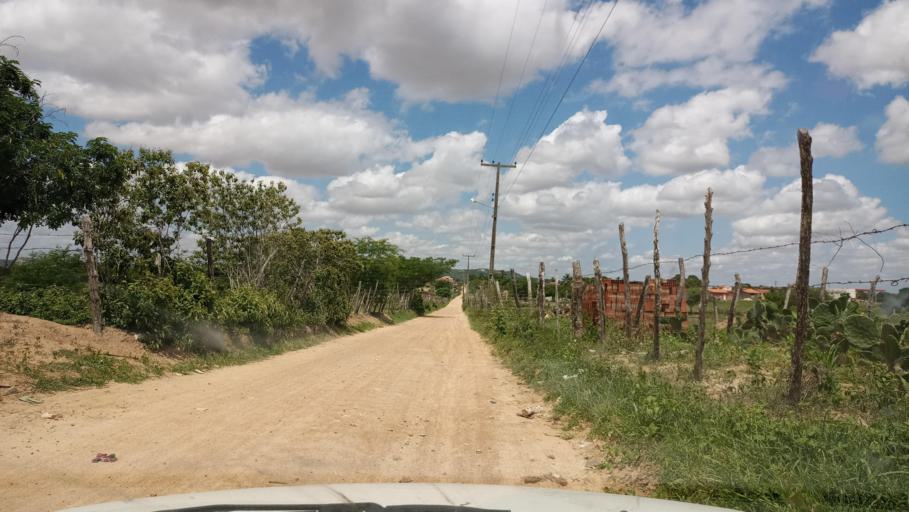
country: BR
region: Rio Grande do Norte
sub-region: Sao Jose Do Campestre
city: Sao Jose do Campestre
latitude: -6.4417
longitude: -35.6299
